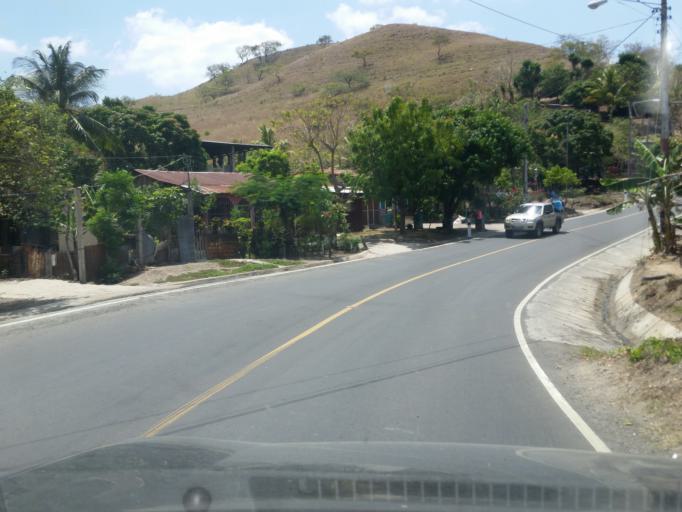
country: NI
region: Boaco
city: Boaco
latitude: 12.4718
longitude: -85.6482
